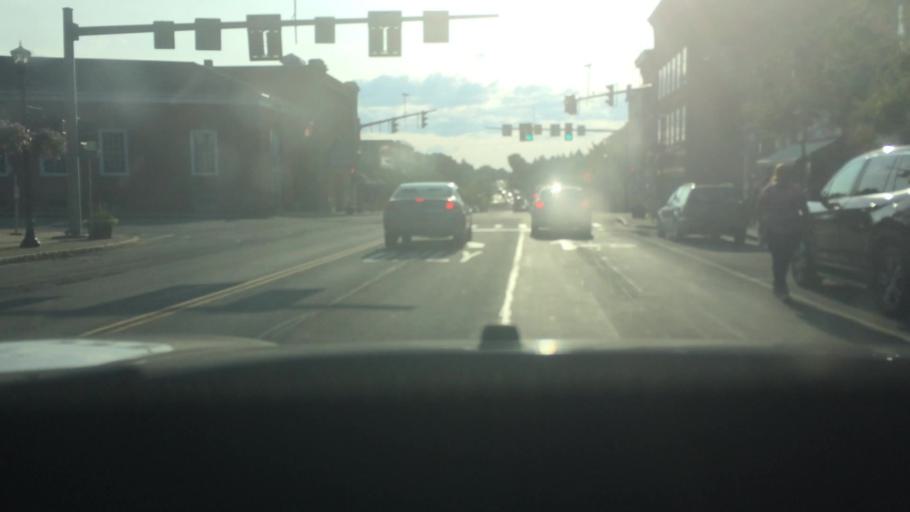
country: US
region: New York
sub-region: St. Lawrence County
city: Canton
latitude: 44.5957
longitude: -75.1686
